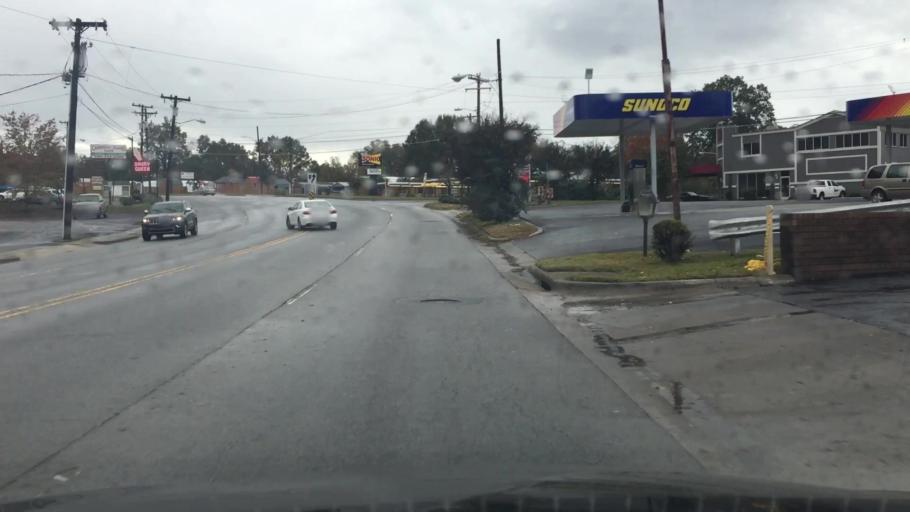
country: US
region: North Carolina
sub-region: Rowan County
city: Salisbury
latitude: 35.6758
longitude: -80.4797
